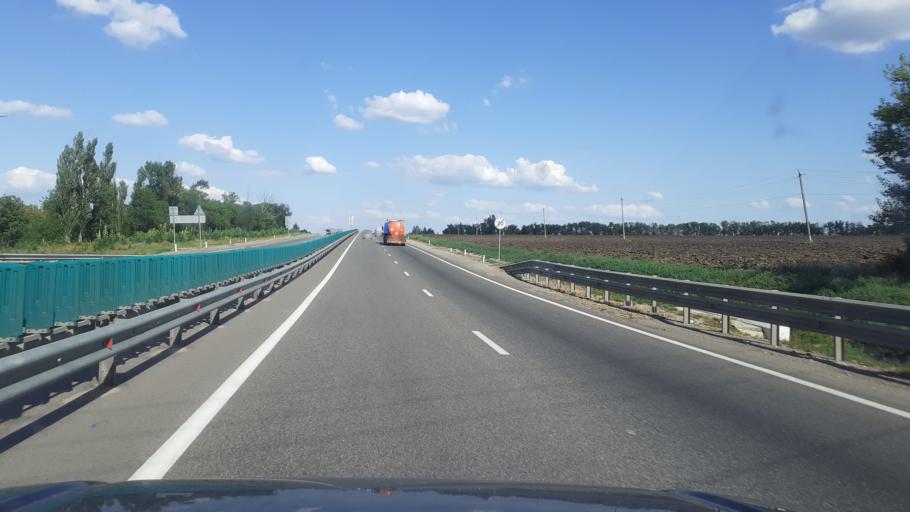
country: RU
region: Krasnodarskiy
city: Severskaya
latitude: 44.8546
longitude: 38.7121
